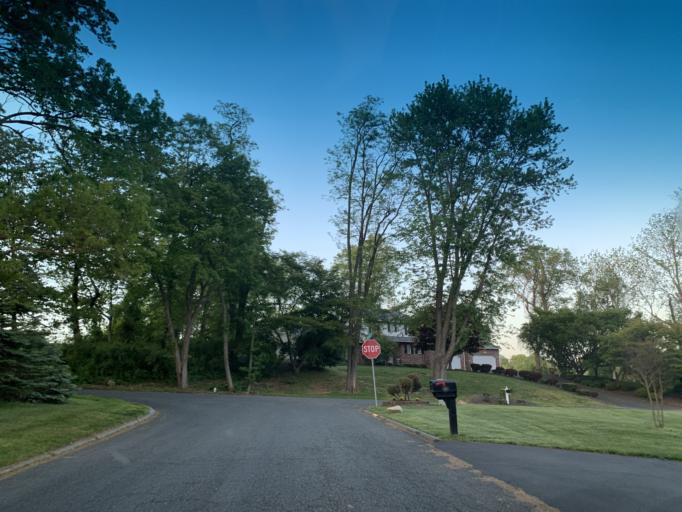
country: US
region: Maryland
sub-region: Harford County
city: South Bel Air
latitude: 39.5662
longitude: -76.2756
